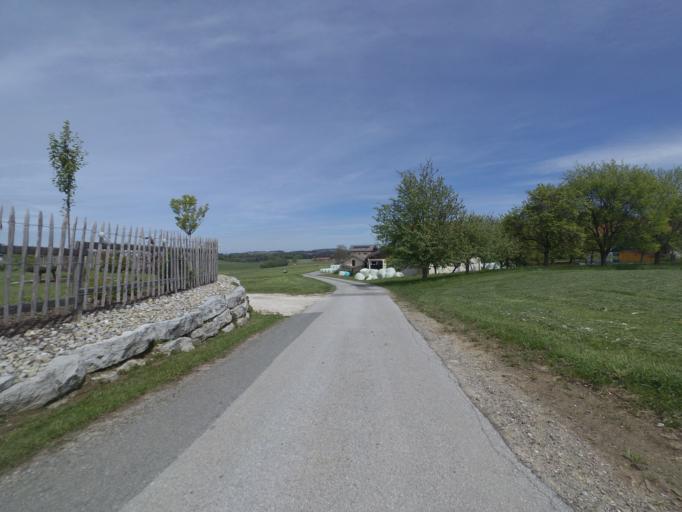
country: AT
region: Salzburg
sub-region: Politischer Bezirk Salzburg-Umgebung
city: Berndorf bei Salzburg
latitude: 47.9902
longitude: 13.0792
